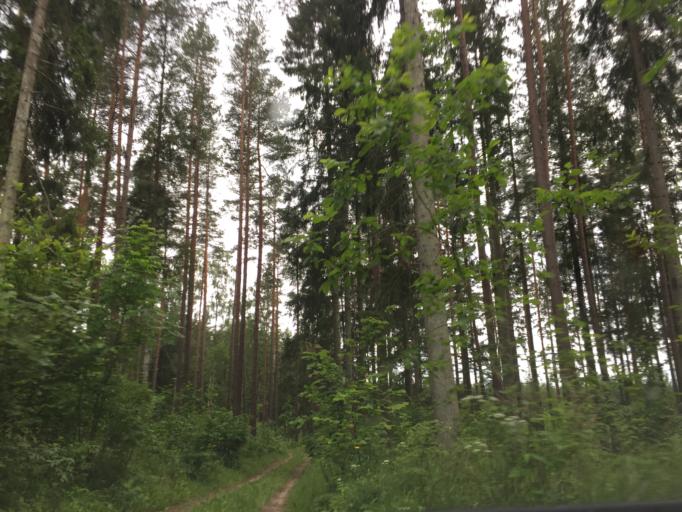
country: LV
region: Tukuma Rajons
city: Tukums
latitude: 57.0263
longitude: 23.0758
